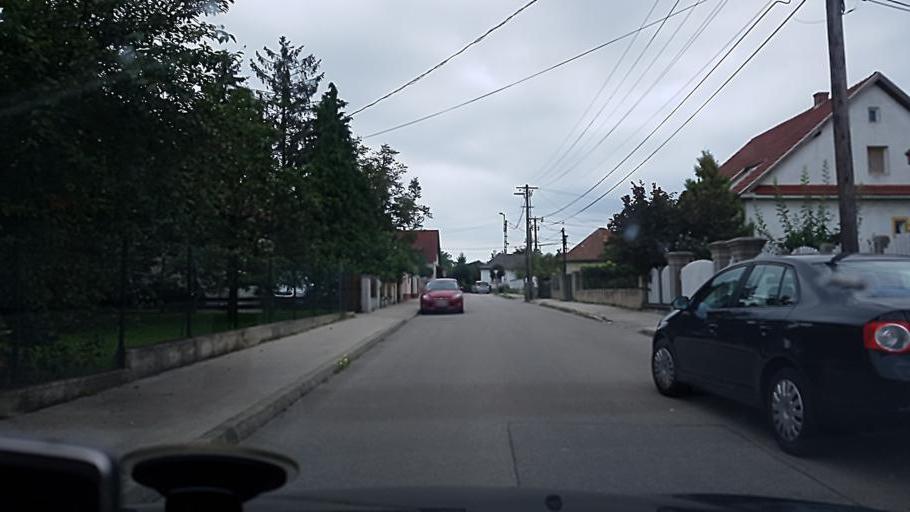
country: HU
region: Veszprem
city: Veszprem
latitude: 47.0937
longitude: 17.9203
